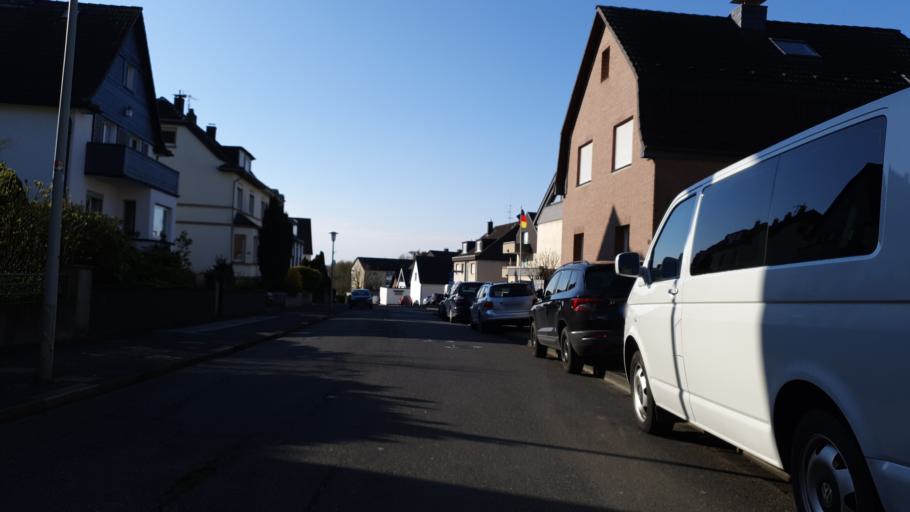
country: DE
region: North Rhine-Westphalia
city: Opladen
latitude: 51.0401
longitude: 7.0470
